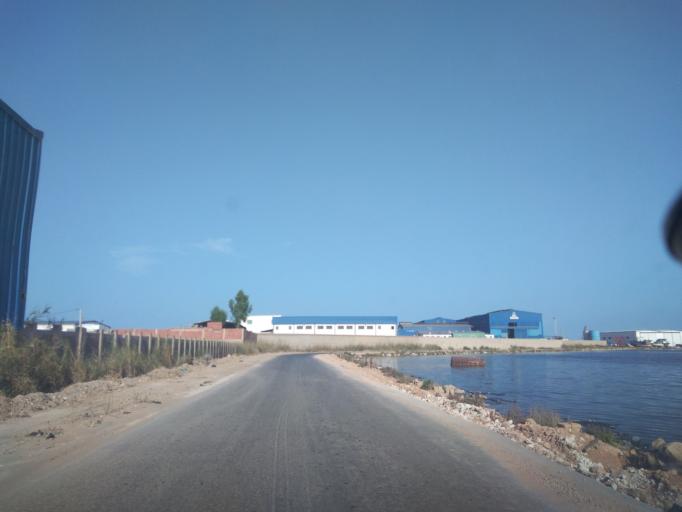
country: TN
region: Safaqis
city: Sfax
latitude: 34.7216
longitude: 10.7644
